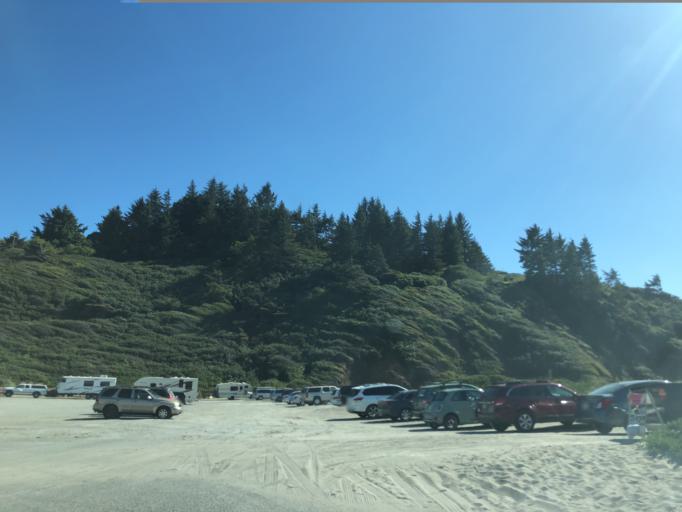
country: US
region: California
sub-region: Humboldt County
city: Westhaven-Moonstone
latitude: 41.0576
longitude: -124.1490
